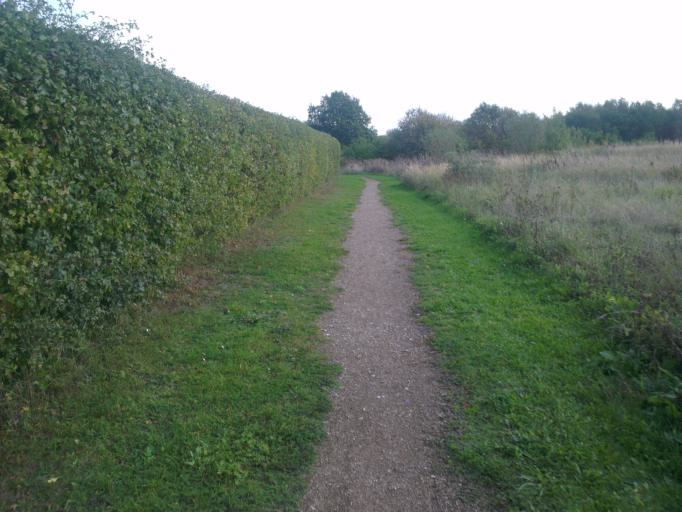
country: DK
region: Capital Region
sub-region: Frederikssund Kommune
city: Frederikssund
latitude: 55.8354
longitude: 12.0889
